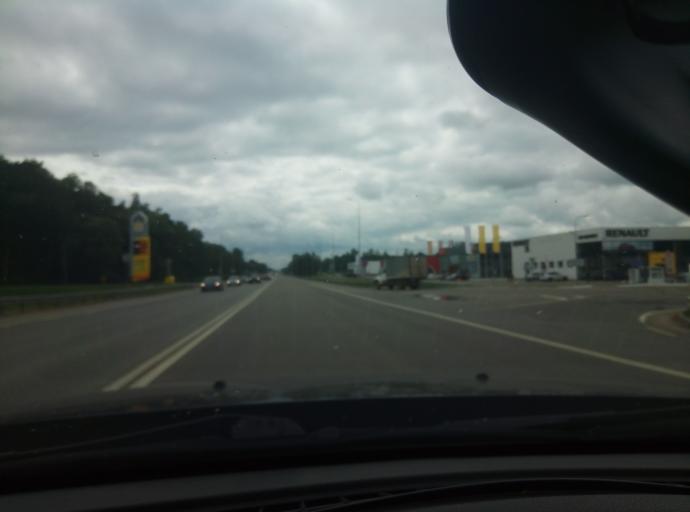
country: RU
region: Kaluga
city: Obninsk
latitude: 55.1050
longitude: 36.6411
